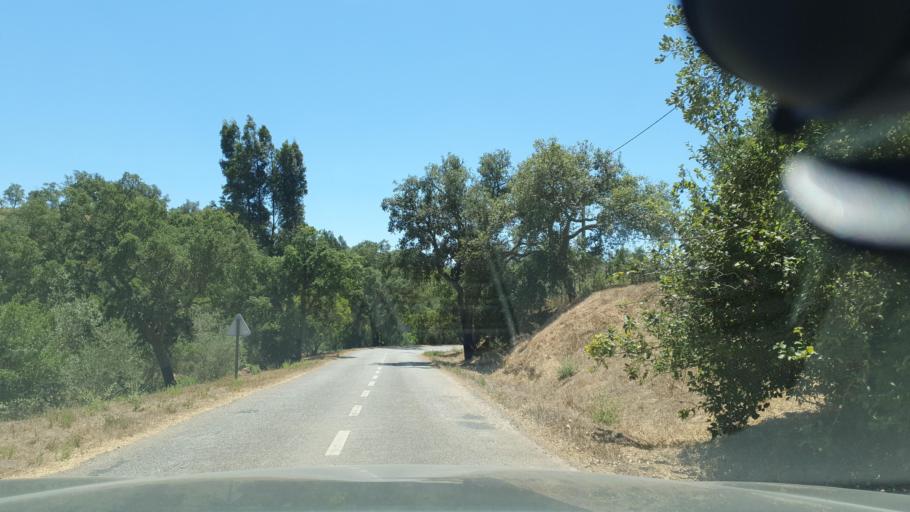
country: PT
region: Beja
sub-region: Odemira
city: Odemira
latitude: 37.6148
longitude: -8.5028
